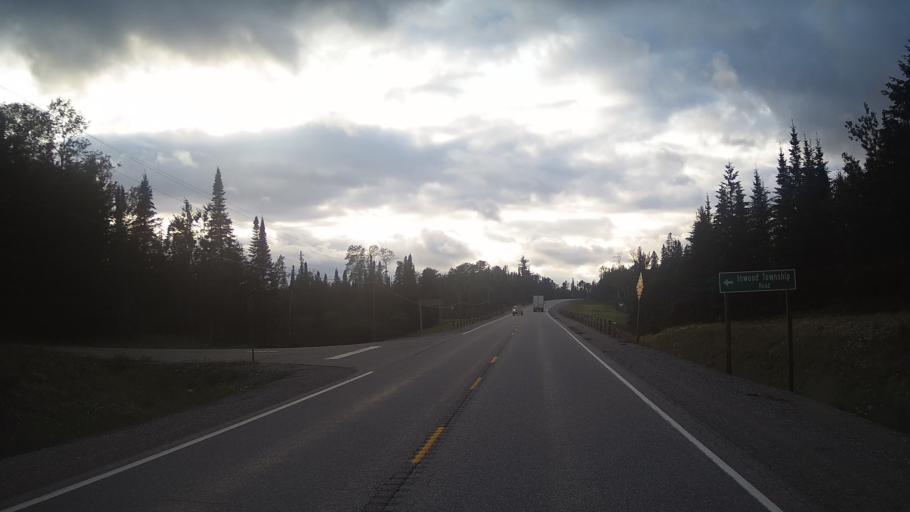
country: CA
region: Ontario
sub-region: Rainy River District
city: Atikokan
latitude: 49.0150
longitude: -90.4325
